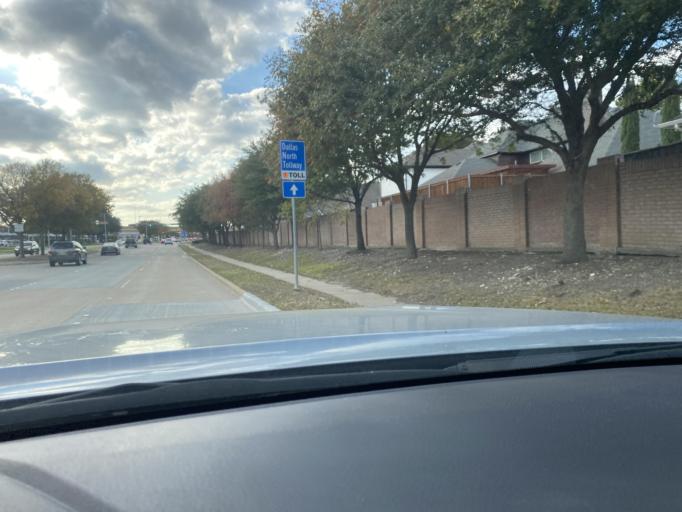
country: US
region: Texas
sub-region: Dallas County
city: Addison
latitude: 33.0167
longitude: -96.8251
